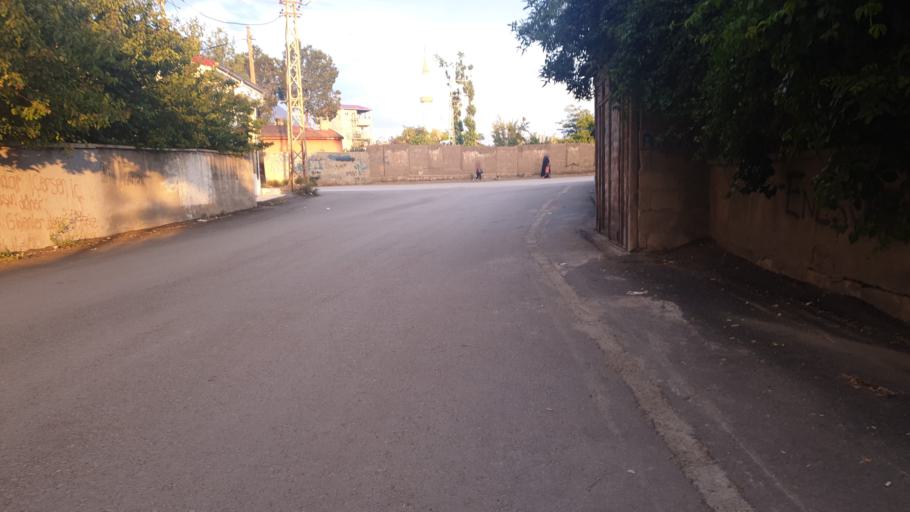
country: TR
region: Van
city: Van
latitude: 38.4883
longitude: 43.3884
